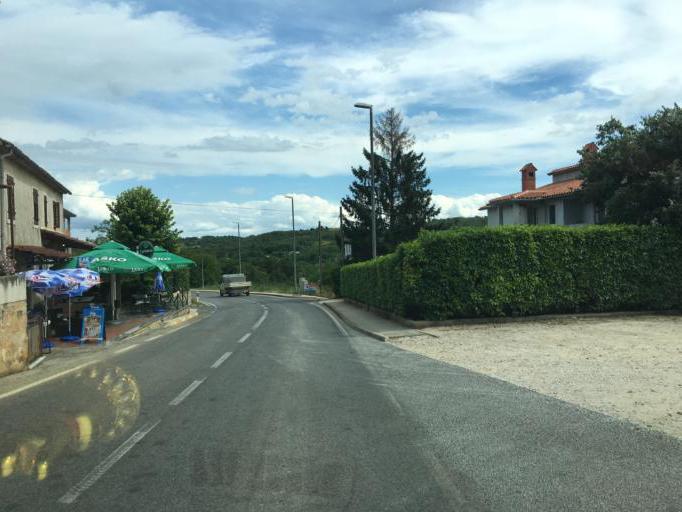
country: HR
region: Istarska
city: Karojba
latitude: 45.2795
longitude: 13.8433
